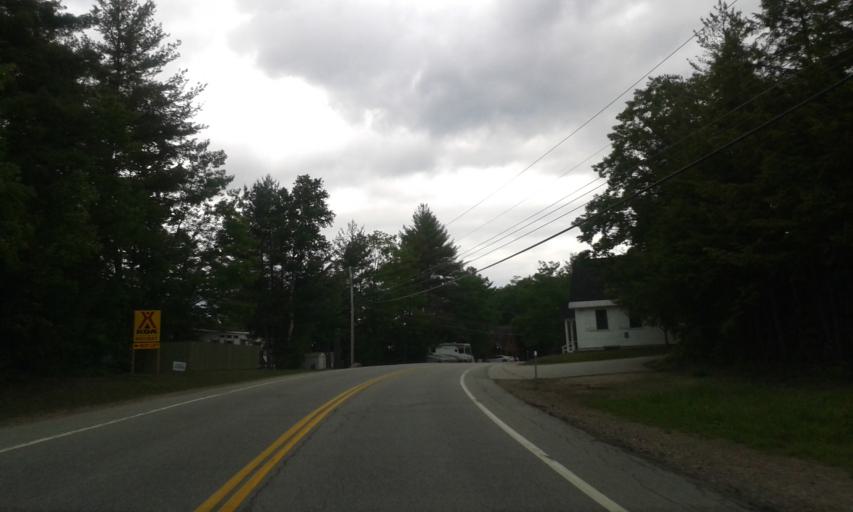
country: US
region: New Hampshire
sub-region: Grafton County
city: Woodstock
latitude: 43.9850
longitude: -71.6822
